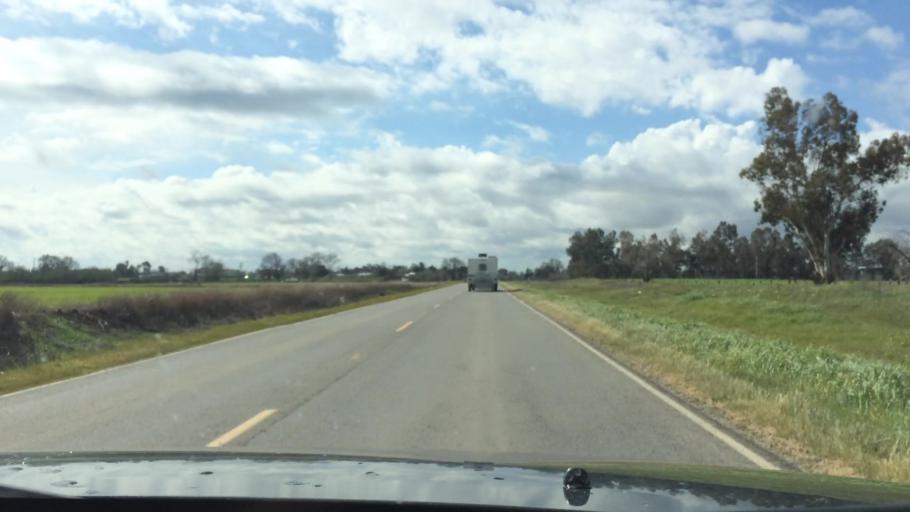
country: US
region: California
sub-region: Sacramento County
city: Herald
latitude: 38.3022
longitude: -121.2327
